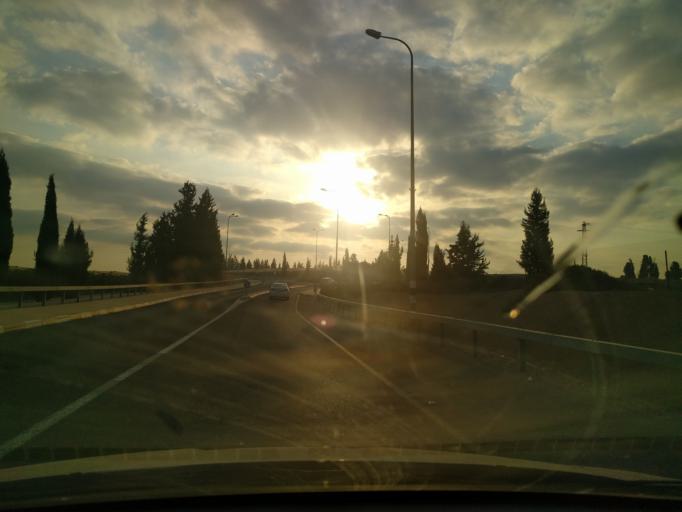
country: IL
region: Haifa
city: Qesarya
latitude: 32.5086
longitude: 34.9337
